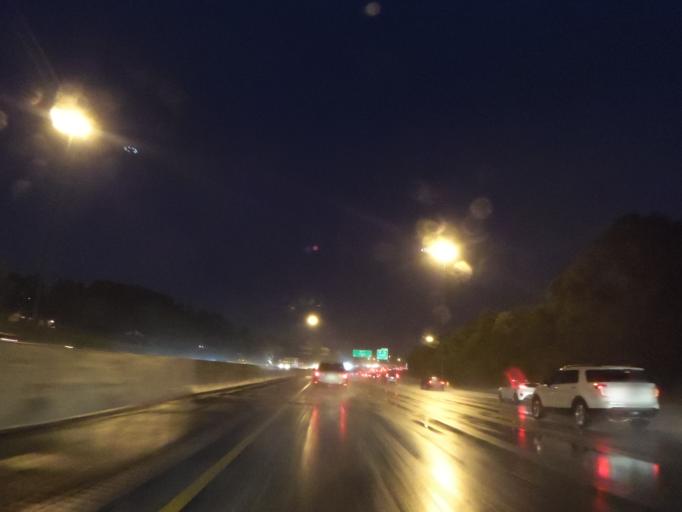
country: US
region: Tennessee
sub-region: Knox County
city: Knoxville
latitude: 35.9448
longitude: -83.9976
